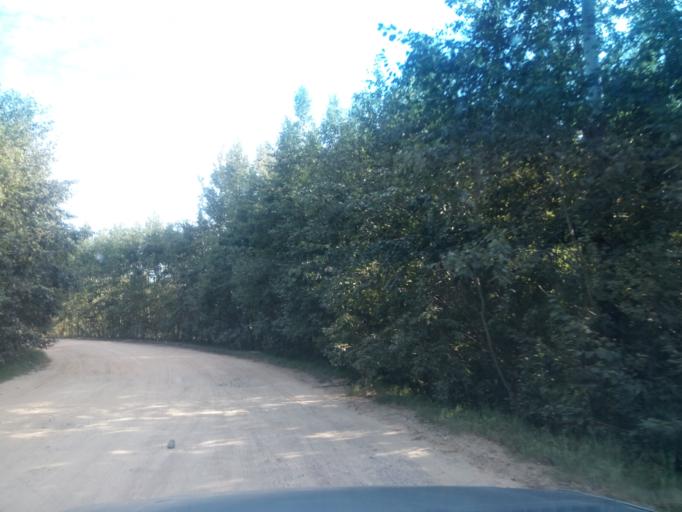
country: BY
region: Vitebsk
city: Polatsk
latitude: 55.4171
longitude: 28.7485
